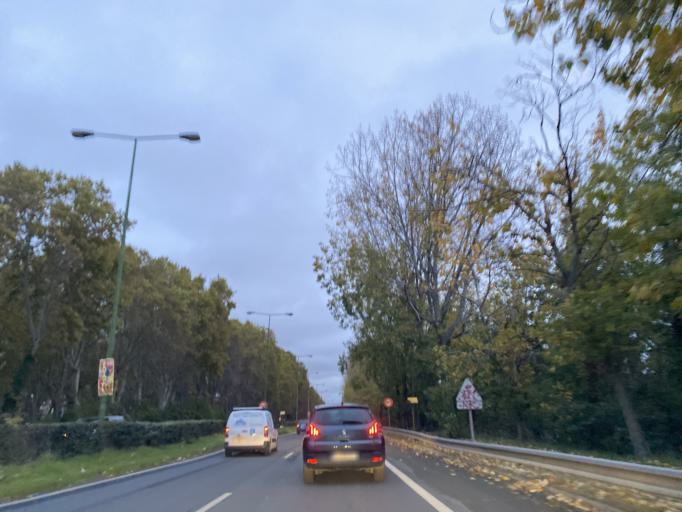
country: FR
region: Ile-de-France
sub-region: Departement du Val-d'Oise
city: Argenteuil
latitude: 48.9369
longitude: 2.2460
